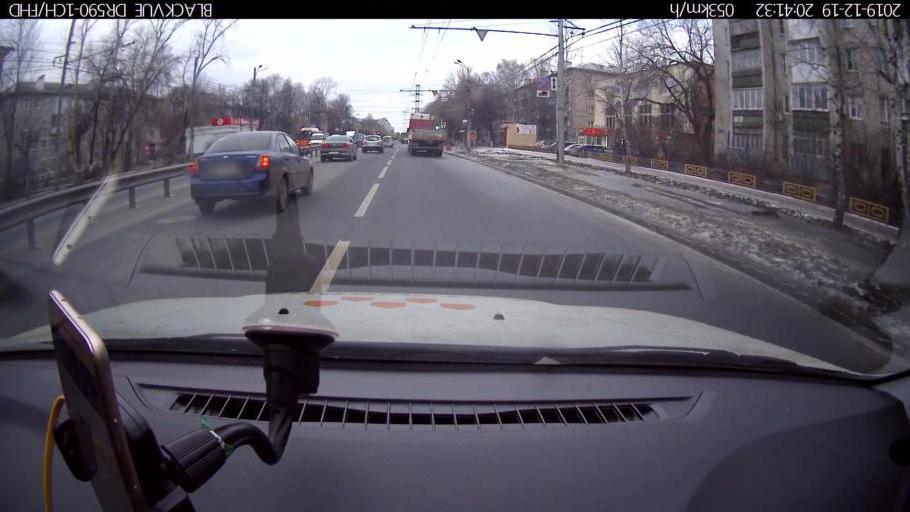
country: RU
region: Nizjnij Novgorod
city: Nizhniy Novgorod
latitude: 56.3186
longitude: 43.8919
